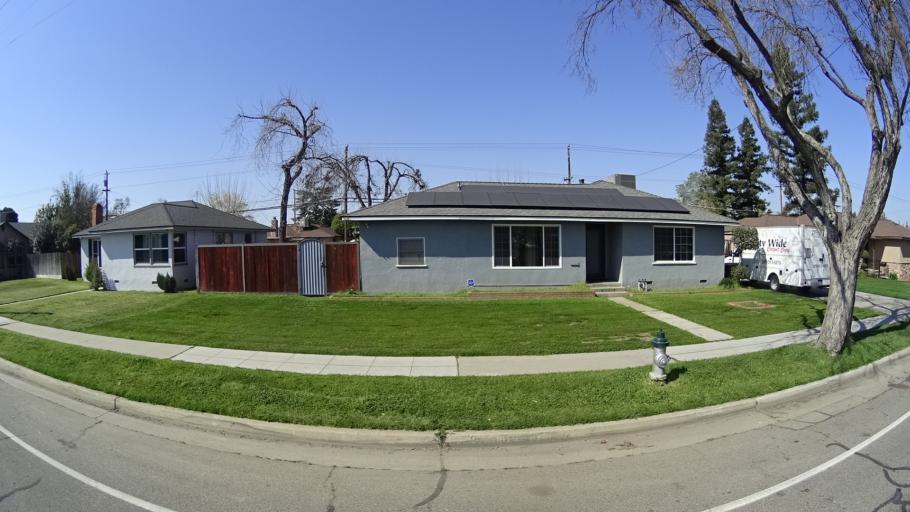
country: US
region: California
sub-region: Fresno County
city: Fresno
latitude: 36.7893
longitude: -119.8266
